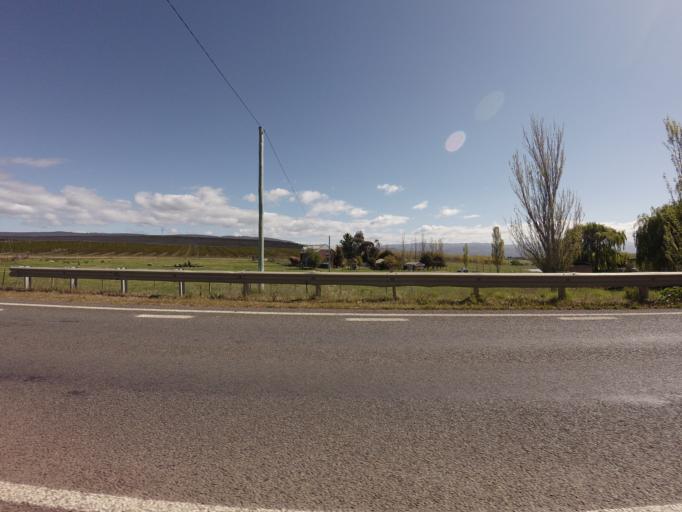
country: AU
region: Tasmania
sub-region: Derwent Valley
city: New Norfolk
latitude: -42.7081
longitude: 146.9453
